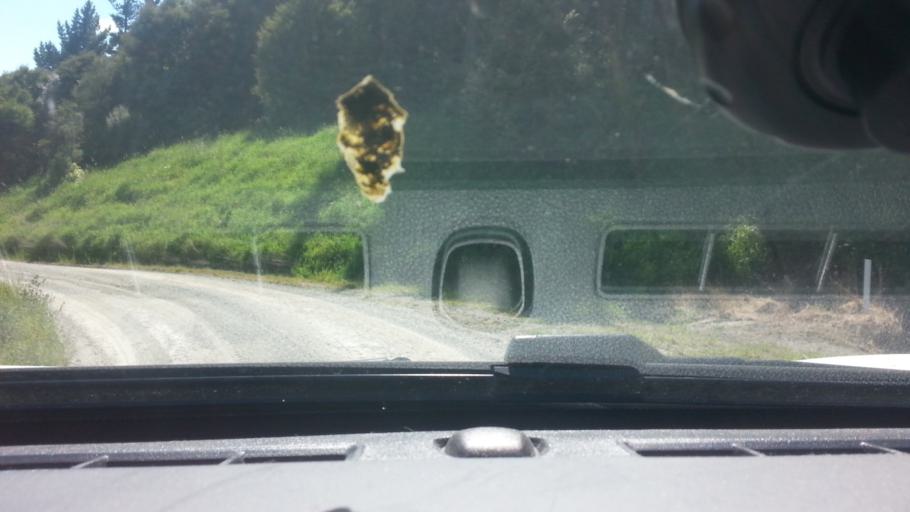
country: NZ
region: Wellington
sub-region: South Wairarapa District
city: Waipawa
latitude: -41.4307
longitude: 175.4662
